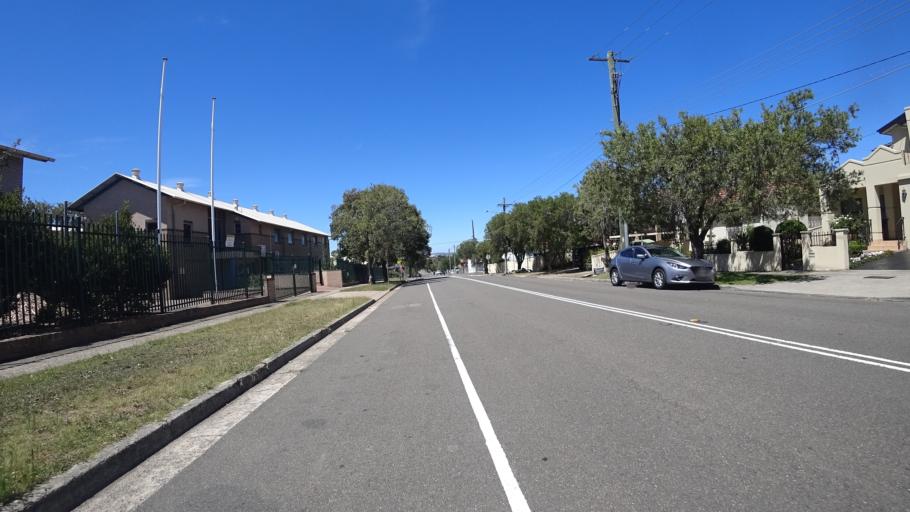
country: AU
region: New South Wales
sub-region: Rockdale
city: Bexley
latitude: -33.9637
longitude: 151.1229
